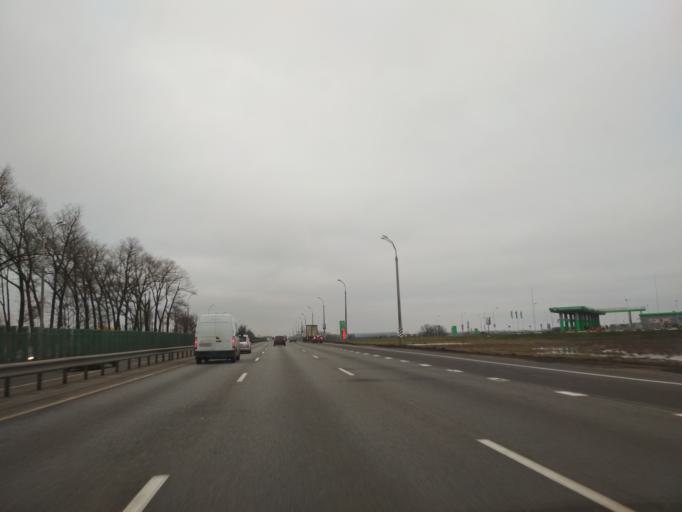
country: BY
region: Minsk
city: Yubilyeyny
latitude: 53.8379
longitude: 27.5113
